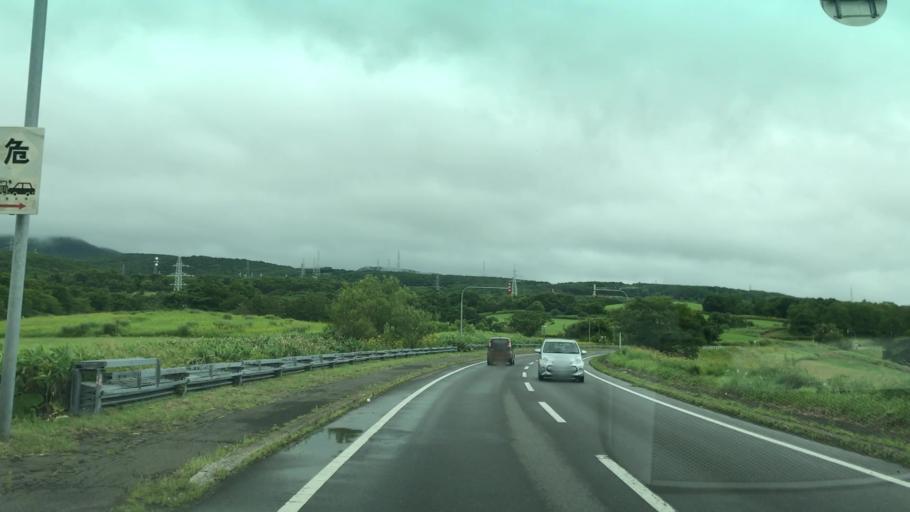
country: JP
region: Hokkaido
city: Muroran
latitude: 42.3889
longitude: 140.9867
